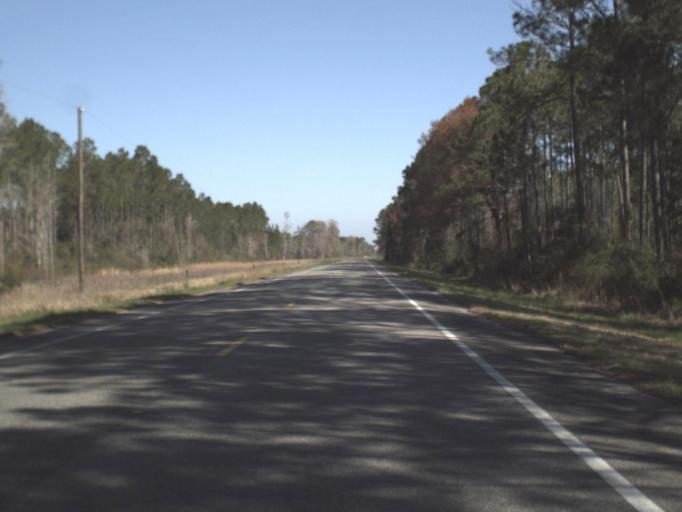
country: US
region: Florida
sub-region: Leon County
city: Woodville
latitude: 30.2483
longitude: -84.0427
